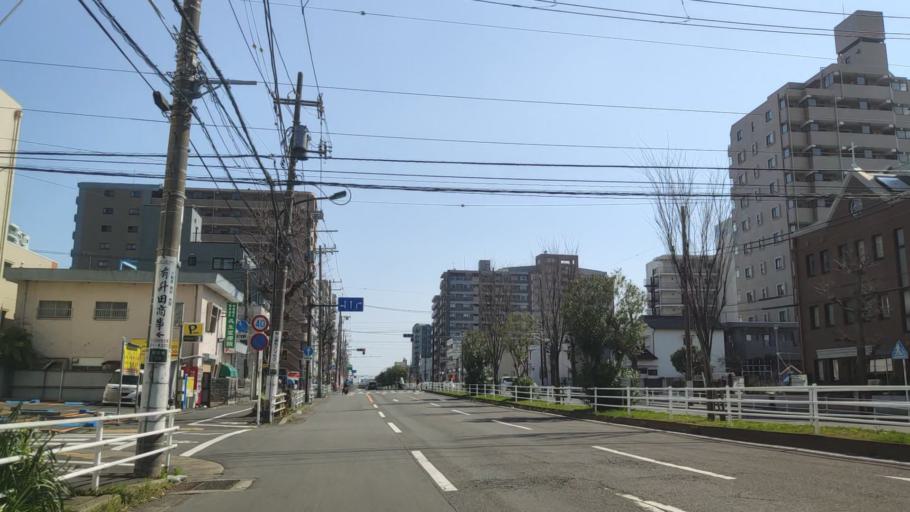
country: JP
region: Kanagawa
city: Hiratsuka
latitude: 35.3319
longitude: 139.3447
